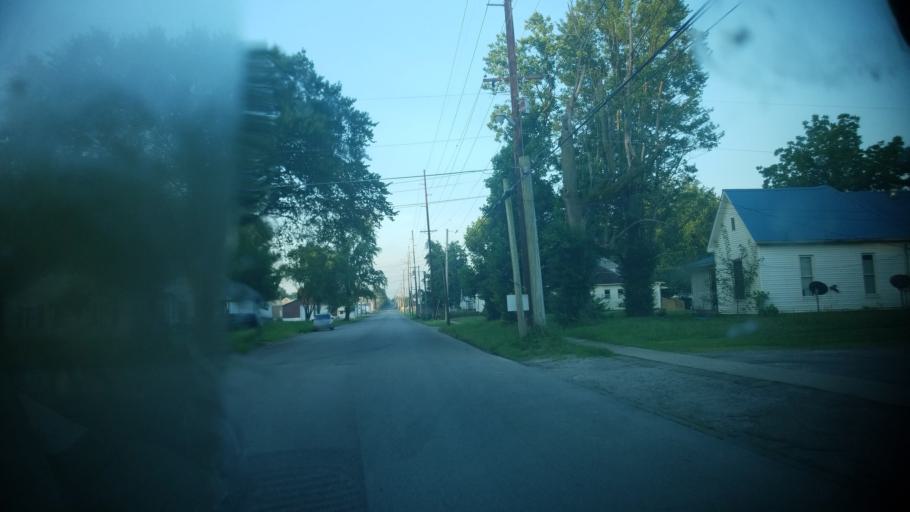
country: US
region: Illinois
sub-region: Wayne County
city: Fairfield
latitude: 38.3831
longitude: -88.3684
